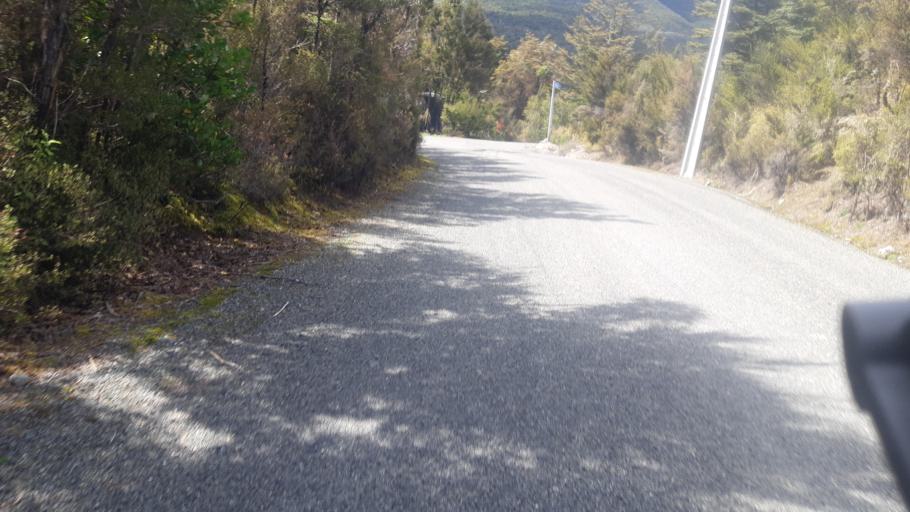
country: NZ
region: Tasman
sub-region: Tasman District
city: Wakefield
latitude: -41.8058
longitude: 172.8399
